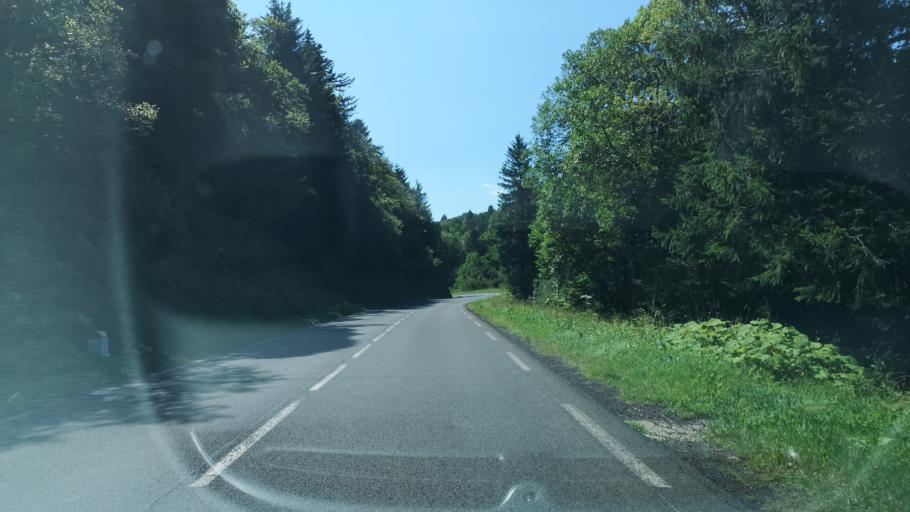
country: FR
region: Auvergne
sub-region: Departement du Puy-de-Dome
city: Mont-Dore
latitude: 45.6084
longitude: 2.8254
